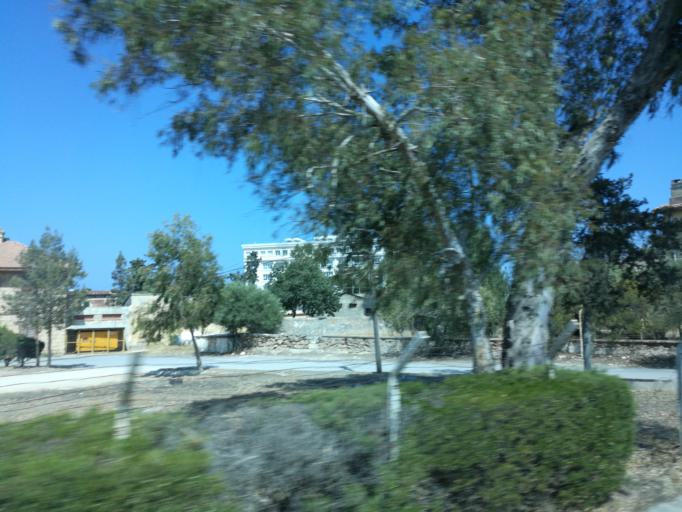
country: CY
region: Ammochostos
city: Famagusta
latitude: 35.1183
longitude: 33.9426
